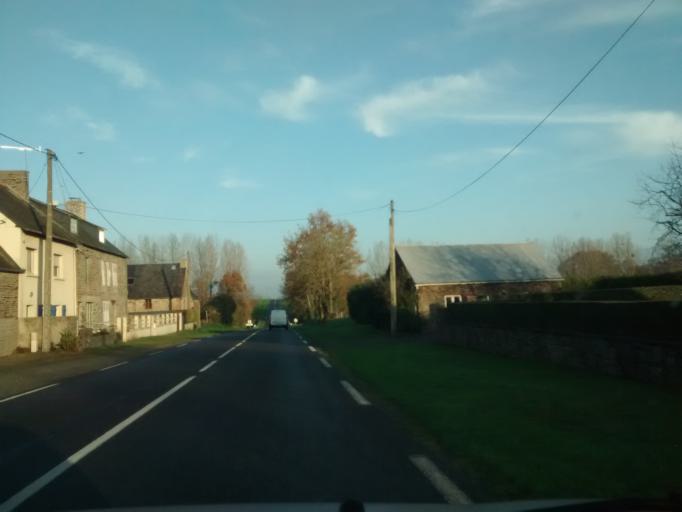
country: FR
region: Lower Normandy
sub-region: Departement de la Manche
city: Pontorson
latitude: 48.5254
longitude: -1.4843
